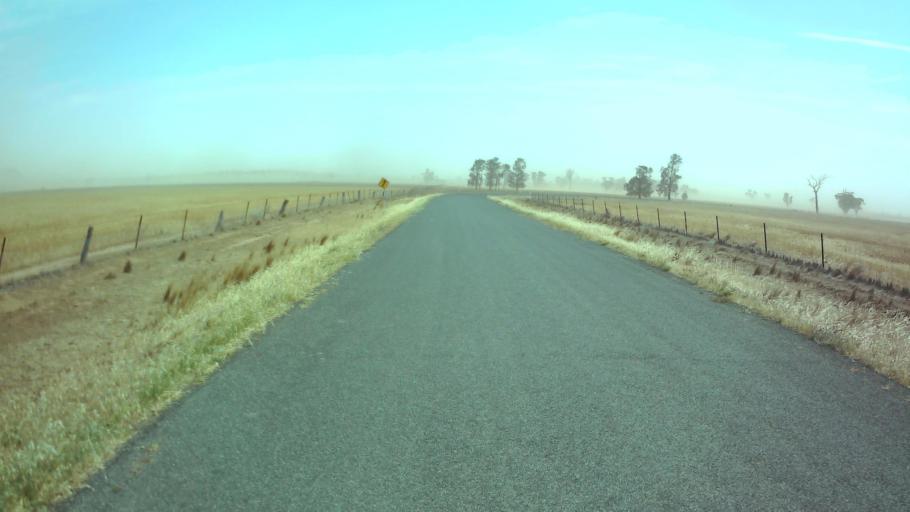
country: AU
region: New South Wales
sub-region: Weddin
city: Grenfell
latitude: -33.7393
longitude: 147.9930
